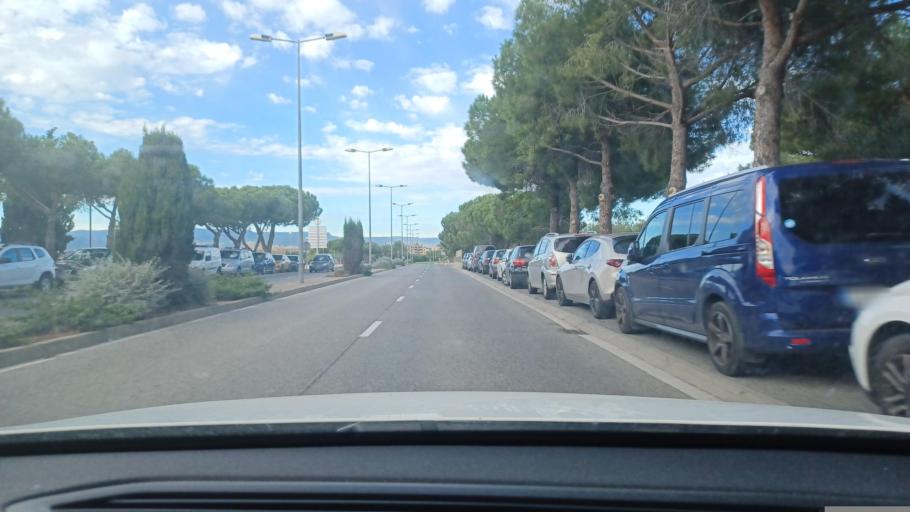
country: ES
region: Catalonia
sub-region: Provincia de Tarragona
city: Vila-seca
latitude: 41.0974
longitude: 1.1520
